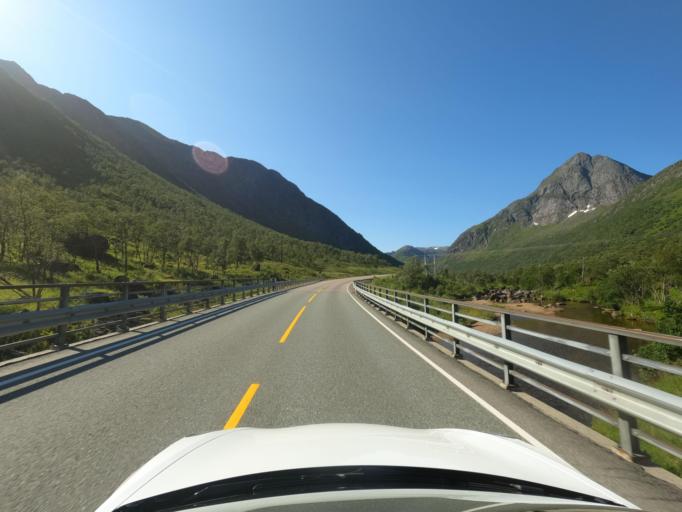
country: NO
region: Nordland
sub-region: Lodingen
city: Lodingen
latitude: 68.5106
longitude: 15.7342
